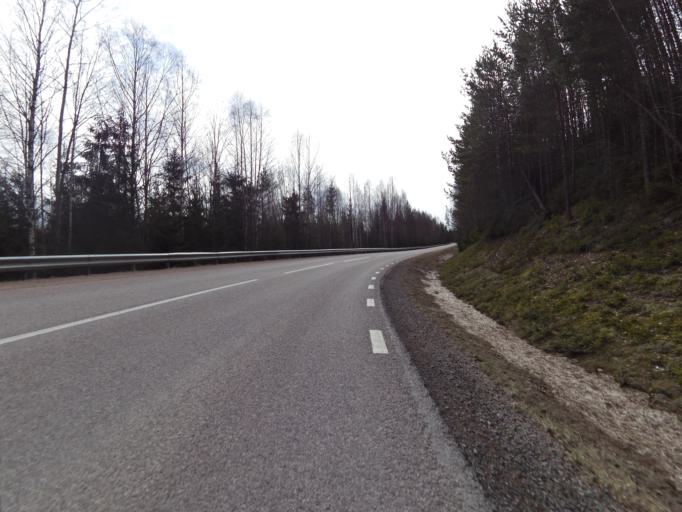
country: SE
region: Dalarna
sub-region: Hedemora Kommun
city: Langshyttan
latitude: 60.5398
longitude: 16.1305
